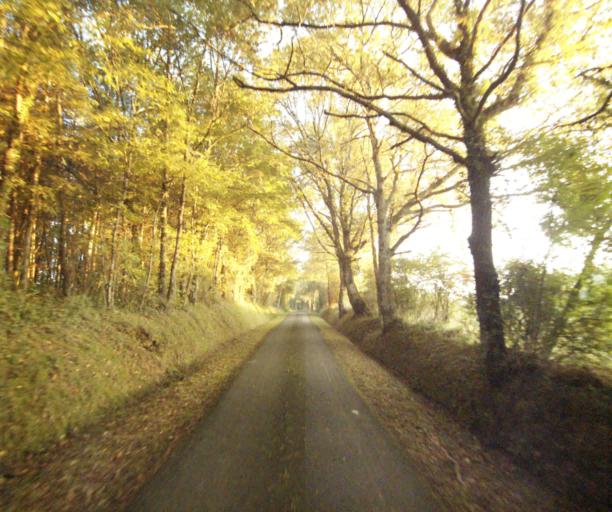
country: FR
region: Midi-Pyrenees
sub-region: Departement du Gers
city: Gondrin
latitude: 43.7940
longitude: 0.1839
